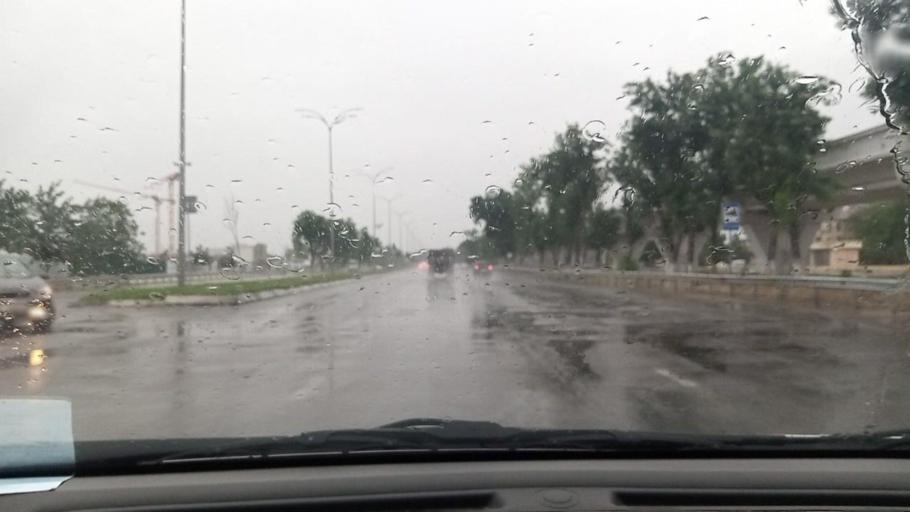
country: UZ
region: Toshkent Shahri
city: Bektemir
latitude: 41.2778
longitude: 69.3613
